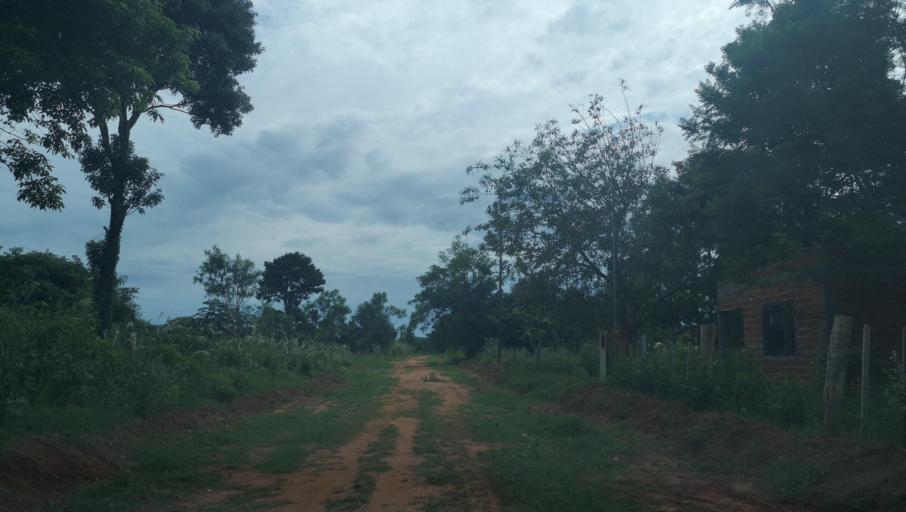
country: PY
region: San Pedro
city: Capiibary
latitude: -24.7230
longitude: -56.0203
